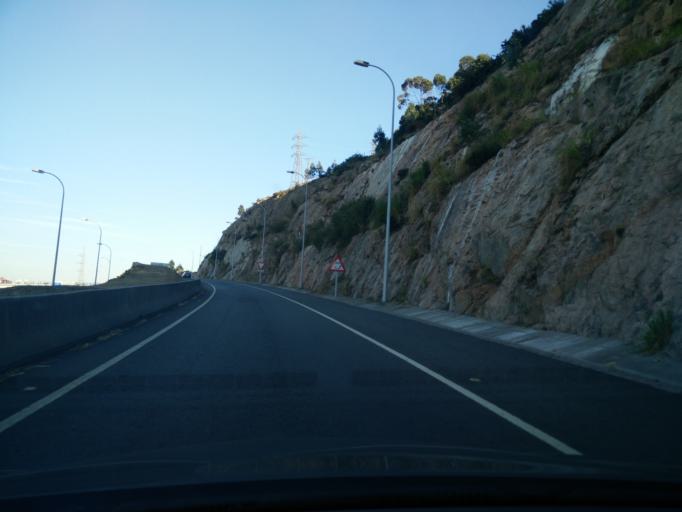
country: ES
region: Galicia
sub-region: Provincia da Coruna
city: A Coruna
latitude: 43.3416
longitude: -8.4309
